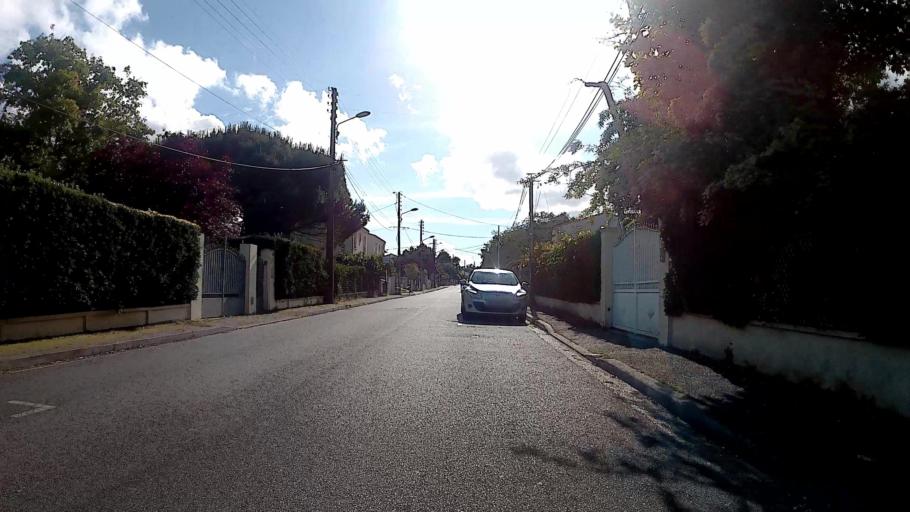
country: FR
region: Aquitaine
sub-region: Departement de la Gironde
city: Pessac
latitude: 44.8180
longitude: -0.6279
